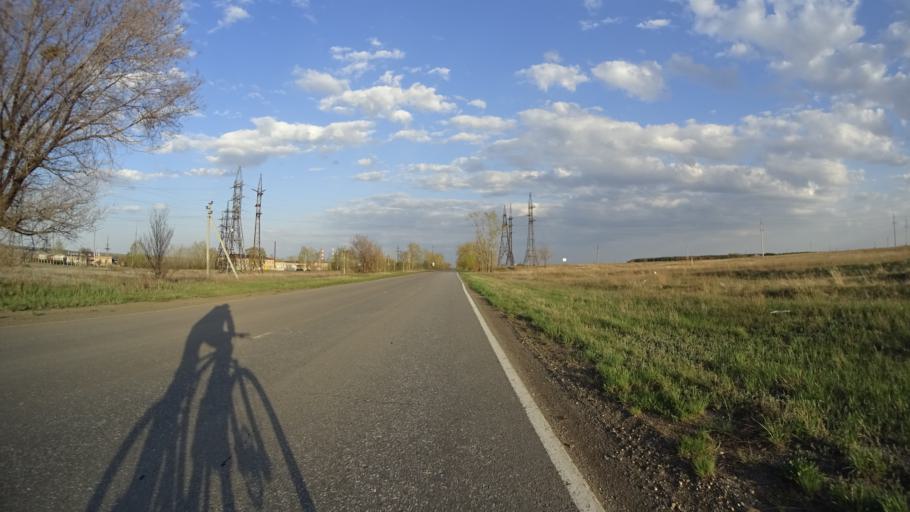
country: RU
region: Chelyabinsk
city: Troitsk
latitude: 54.0575
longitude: 61.5833
